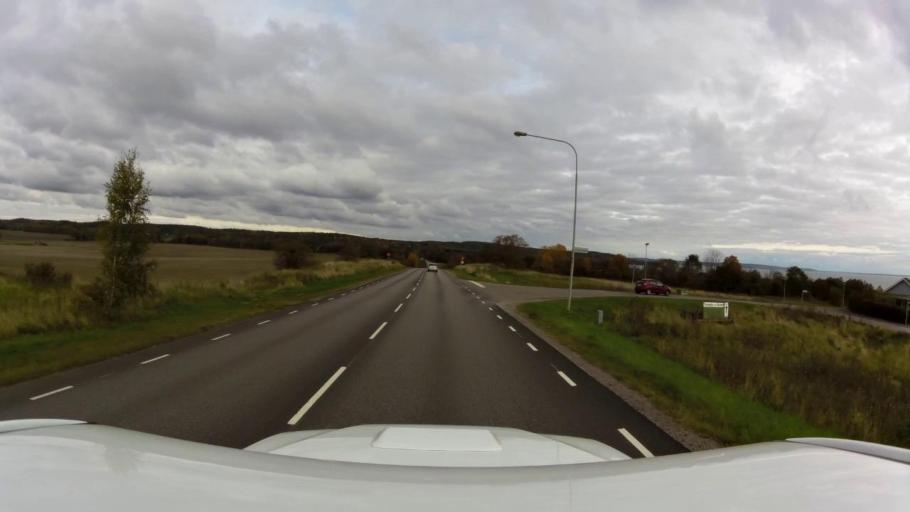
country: SE
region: OEstergoetland
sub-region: Linkopings Kommun
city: Berg
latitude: 58.4946
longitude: 15.5313
